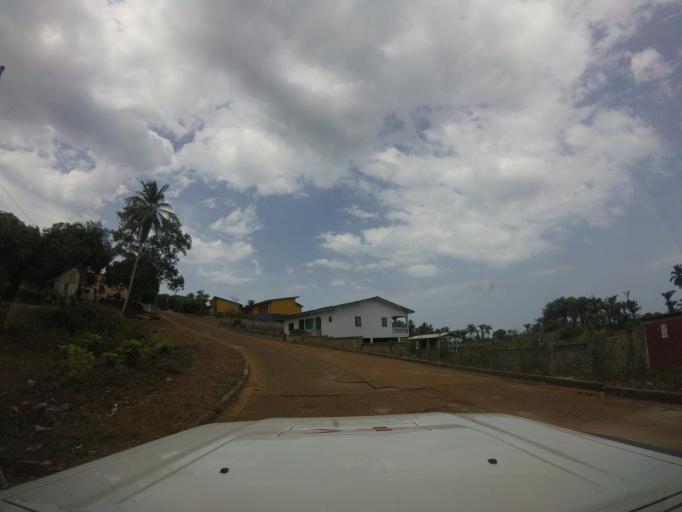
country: LR
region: Grand Cape Mount
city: Robertsport
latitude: 6.7542
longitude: -11.3738
